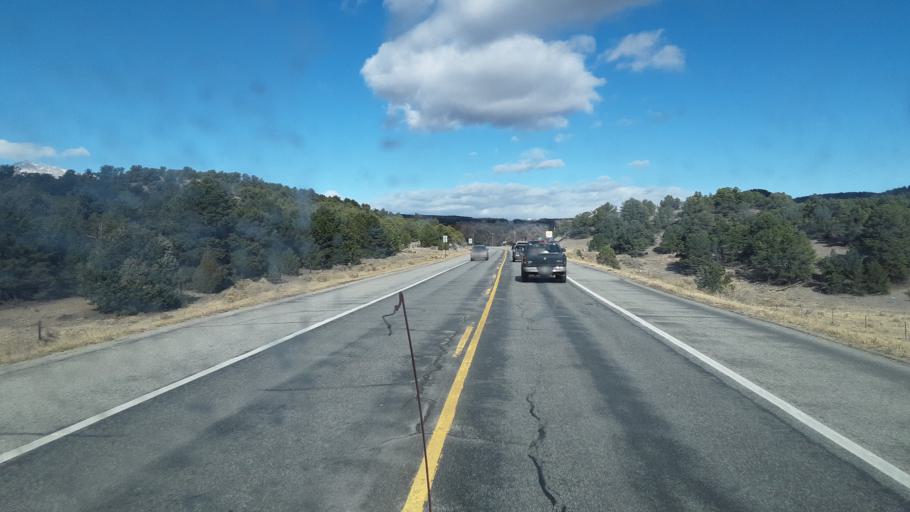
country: US
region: Colorado
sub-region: Chaffee County
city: Salida
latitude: 38.6313
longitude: -106.0790
